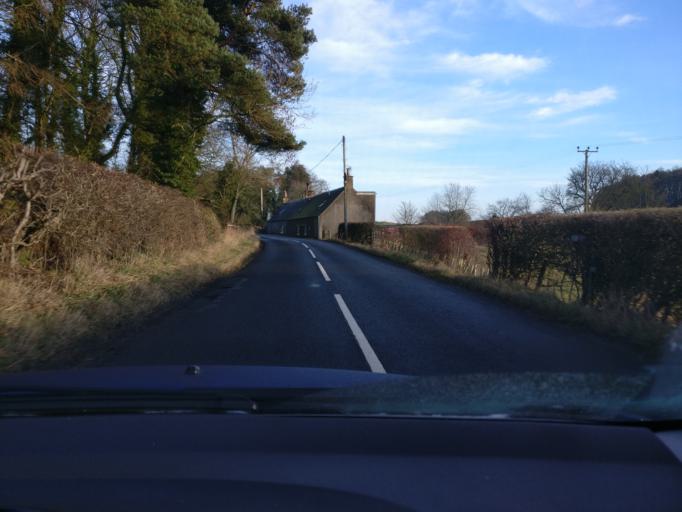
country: GB
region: Scotland
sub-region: The Scottish Borders
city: Hawick
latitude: 55.4446
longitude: -2.7664
